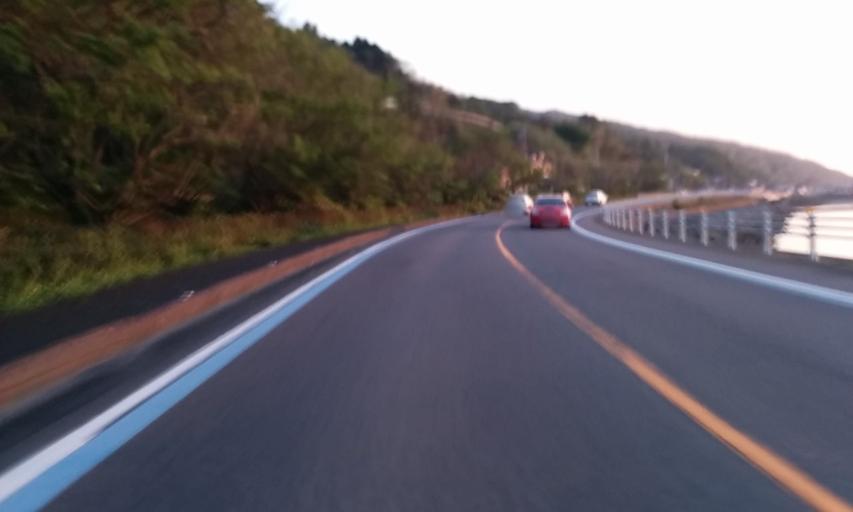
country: JP
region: Ehime
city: Iyo
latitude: 33.6538
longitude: 132.5863
